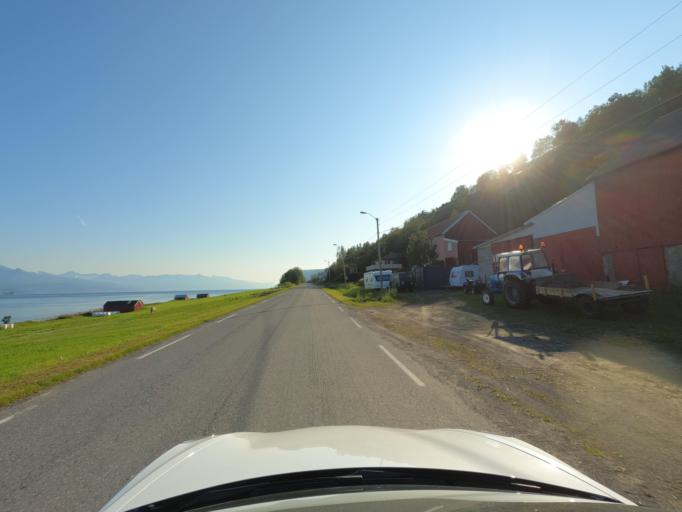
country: NO
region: Nordland
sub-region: Narvik
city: Narvik
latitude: 68.5287
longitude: 17.4614
